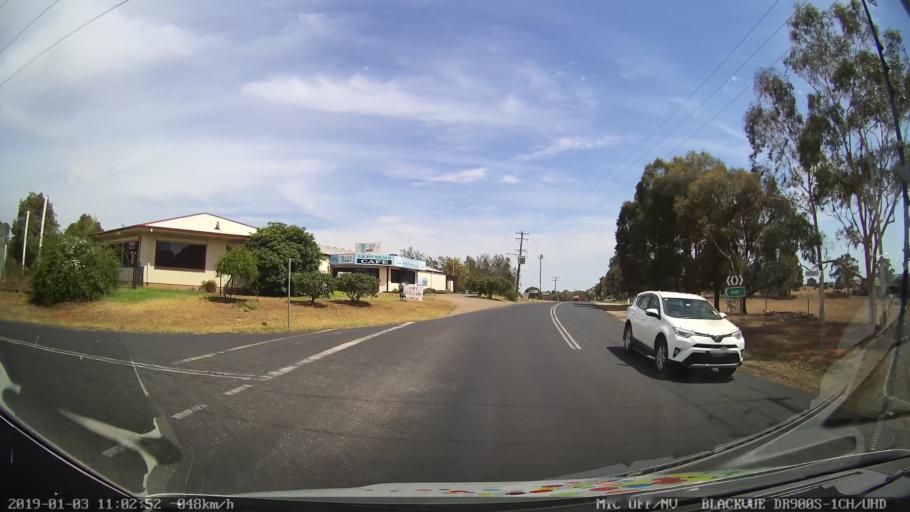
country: AU
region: New South Wales
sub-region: Young
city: Young
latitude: -34.2949
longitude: 148.2973
